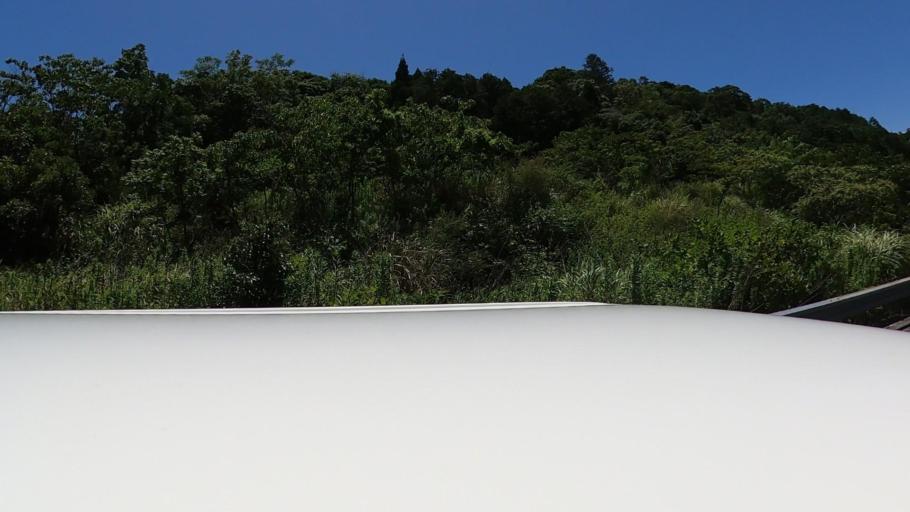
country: JP
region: Miyazaki
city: Nobeoka
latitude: 32.5385
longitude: 131.6590
